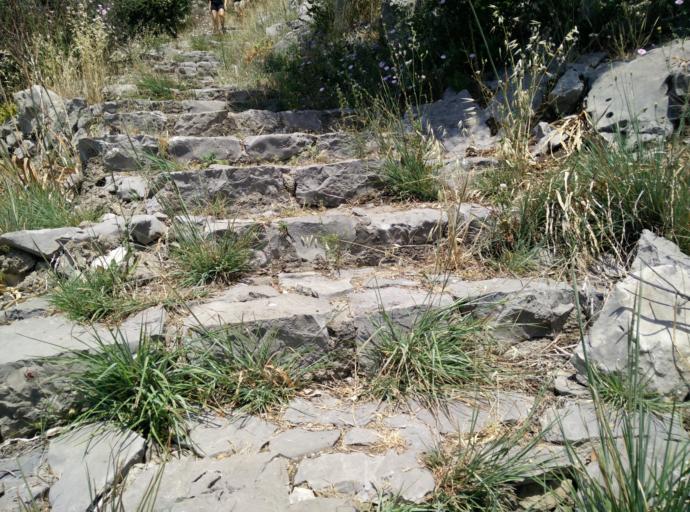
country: IT
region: Campania
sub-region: Provincia di Napoli
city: Massa Lubrense
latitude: 40.5931
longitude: 14.3796
